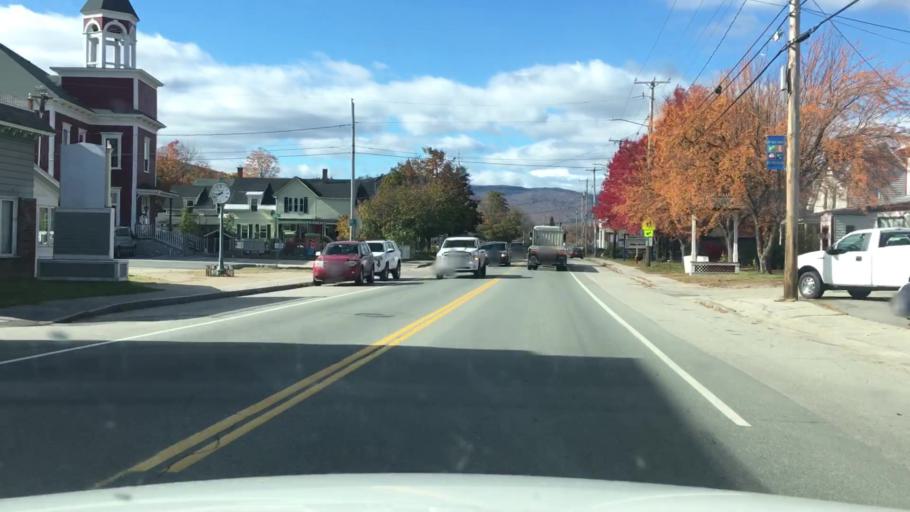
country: US
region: New Hampshire
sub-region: Coos County
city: Gorham
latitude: 44.3892
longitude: -71.1774
